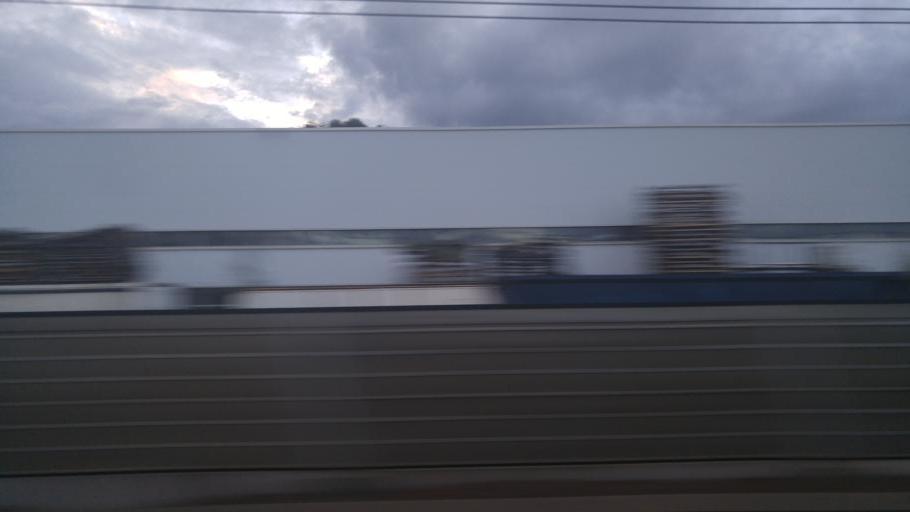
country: NO
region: Akershus
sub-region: Skedsmo
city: Lillestrom
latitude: 59.9660
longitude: 11.0666
